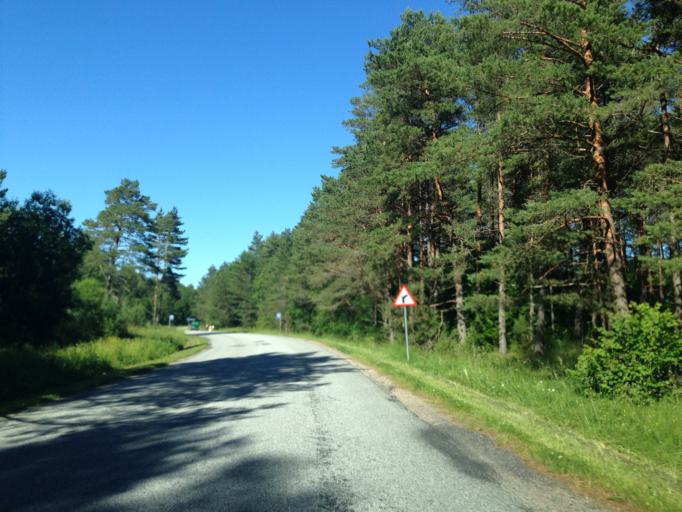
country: EE
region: Harju
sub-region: Raasiku vald
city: Raasiku
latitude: 59.4630
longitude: 25.2383
